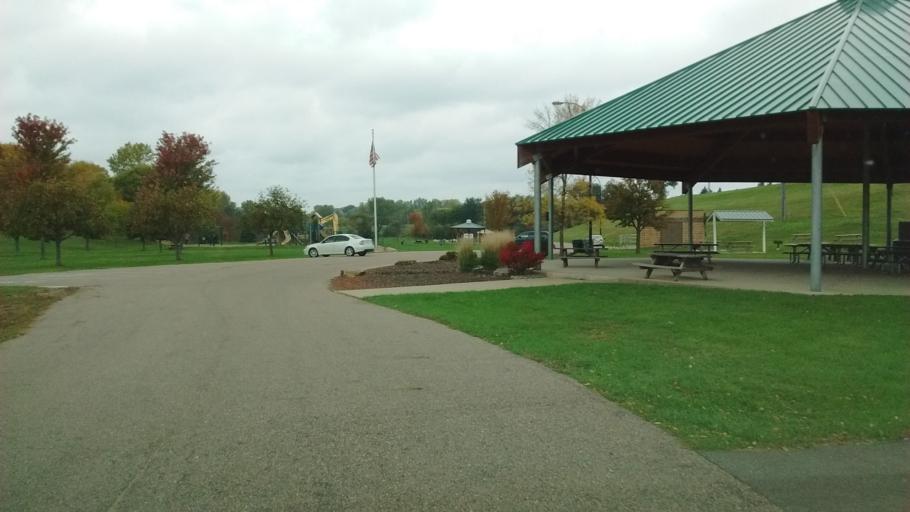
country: US
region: Iowa
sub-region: Woodbury County
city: Sergeant Bluff
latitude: 42.4404
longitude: -96.3517
